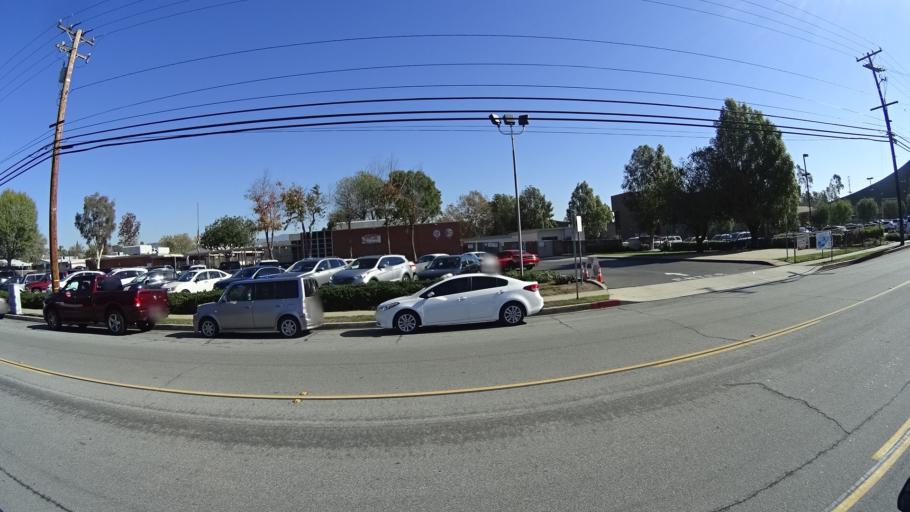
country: US
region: California
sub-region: Orange County
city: Tustin
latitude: 33.7616
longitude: -117.8206
